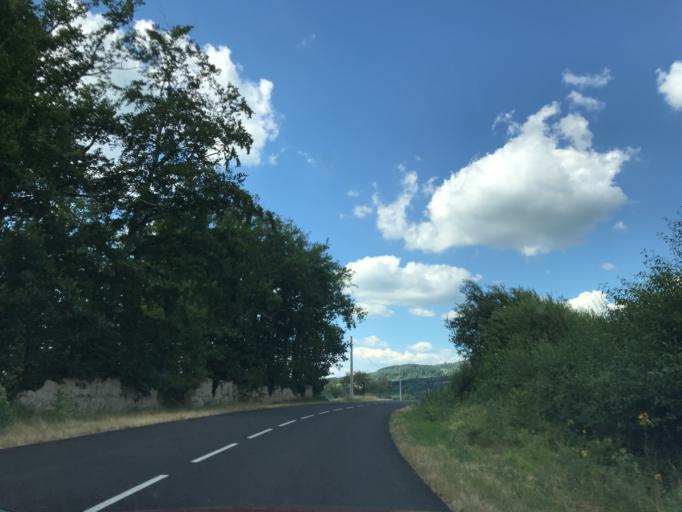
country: FR
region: Auvergne
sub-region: Departement du Puy-de-Dome
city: Courpiere
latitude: 45.7525
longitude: 3.6041
